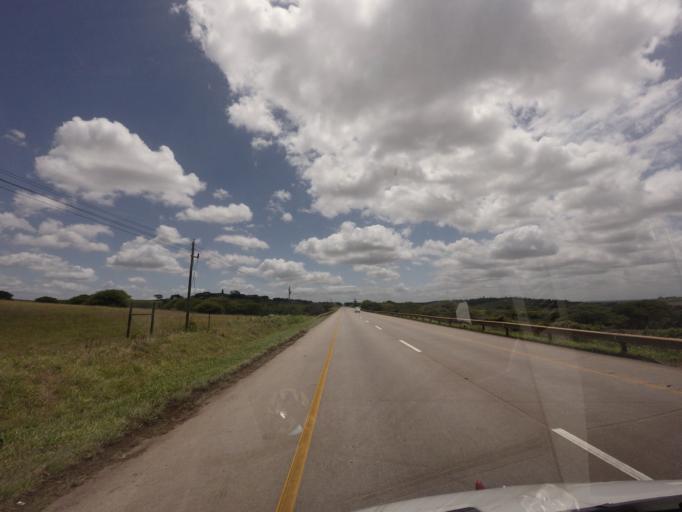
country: ZA
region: KwaZulu-Natal
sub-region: uMkhanyakude District Municipality
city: Mtubatuba
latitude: -28.4923
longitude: 32.1404
